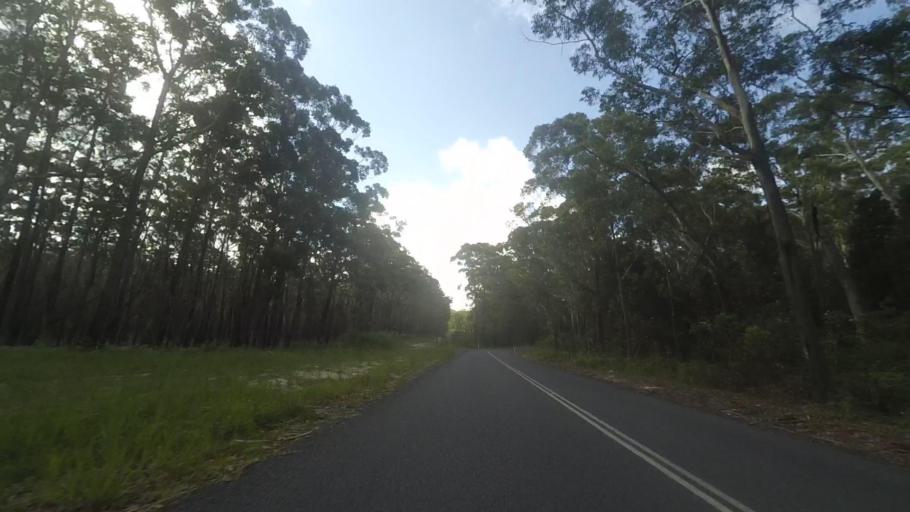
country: AU
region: New South Wales
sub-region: Great Lakes
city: Forster
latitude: -32.4267
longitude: 152.5008
